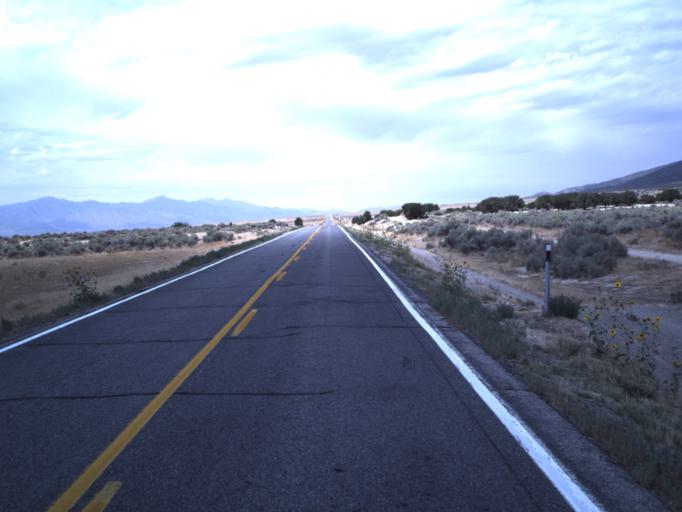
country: US
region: Utah
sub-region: Utah County
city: Eagle Mountain
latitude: 40.2370
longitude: -112.2001
